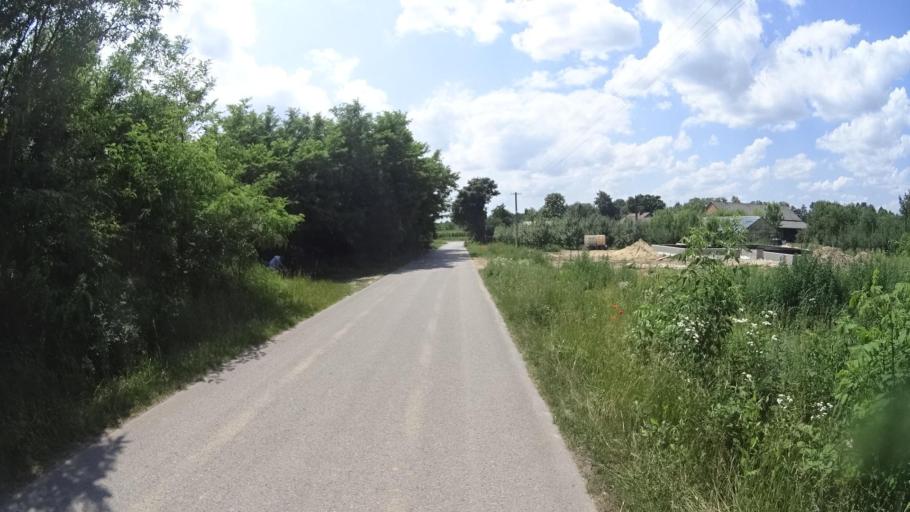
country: PL
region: Masovian Voivodeship
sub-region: Powiat grojecki
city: Goszczyn
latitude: 51.7123
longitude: 20.8898
